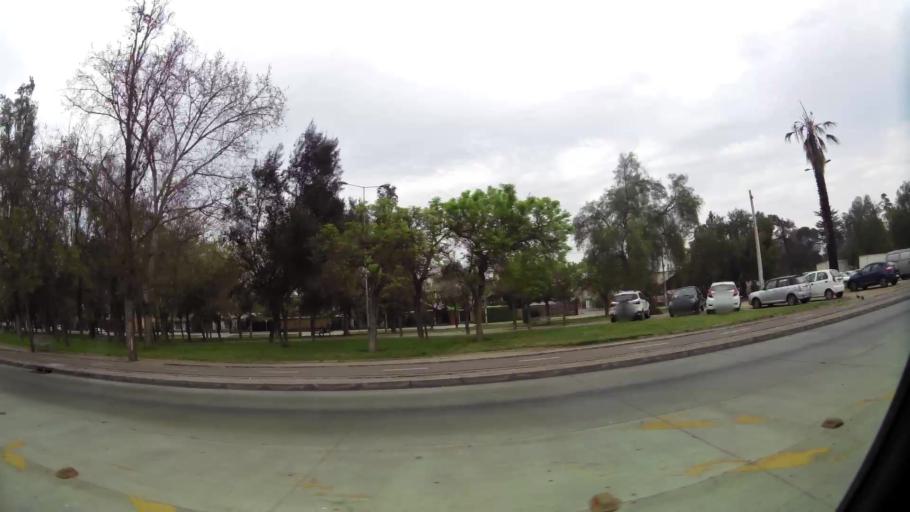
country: CL
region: Santiago Metropolitan
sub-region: Provincia de Santiago
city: Lo Prado
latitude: -33.5105
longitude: -70.7489
